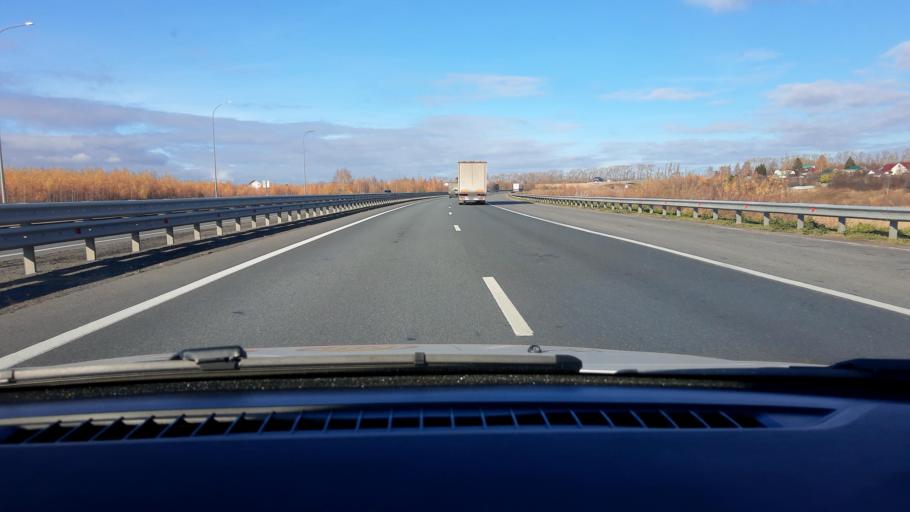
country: RU
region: Nizjnij Novgorod
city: Burevestnik
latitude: 56.1433
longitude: 43.7567
